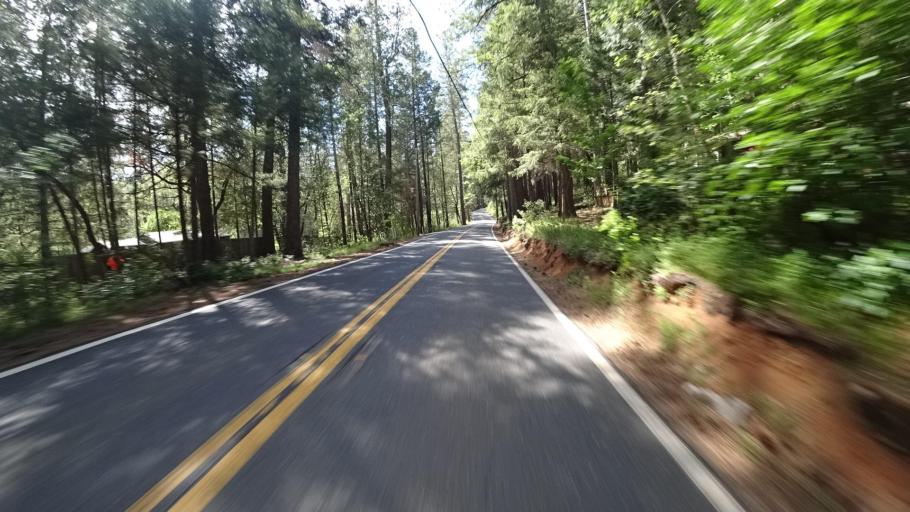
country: US
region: California
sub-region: Lake County
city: Cobb
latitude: 38.8876
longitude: -122.7298
